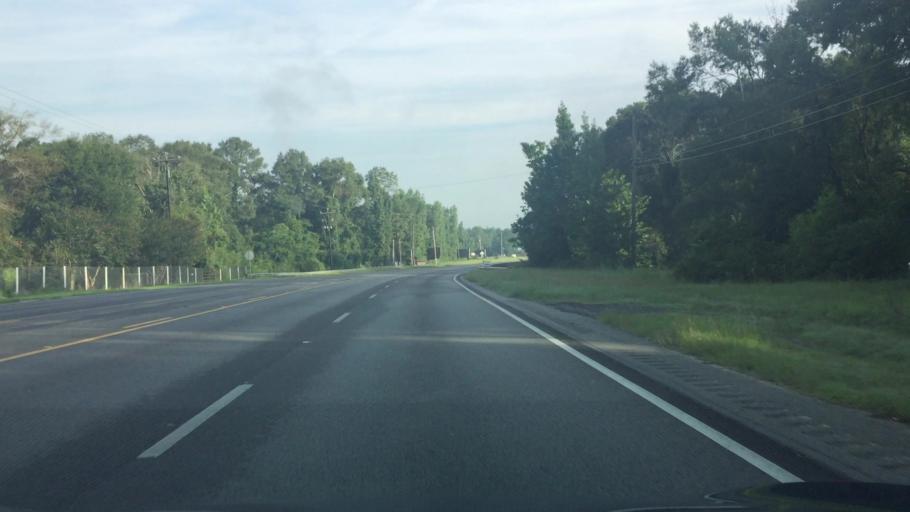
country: US
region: Alabama
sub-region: Covington County
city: Andalusia
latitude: 31.3372
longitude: -86.5211
